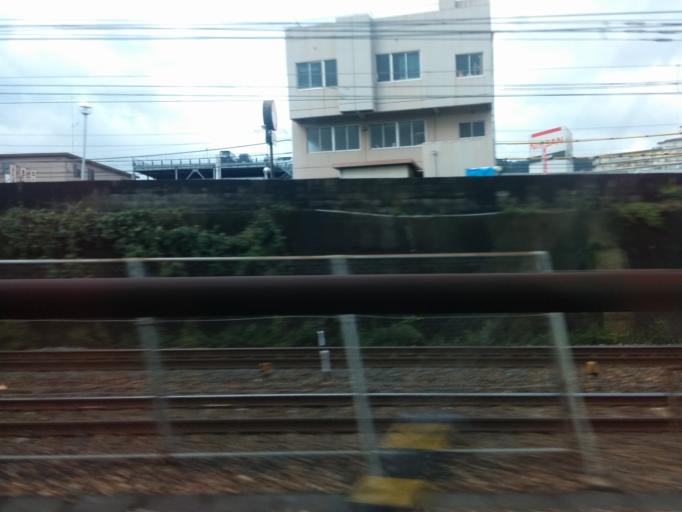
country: JP
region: Shiga Prefecture
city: Otsu-shi
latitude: 34.9945
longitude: 135.8848
